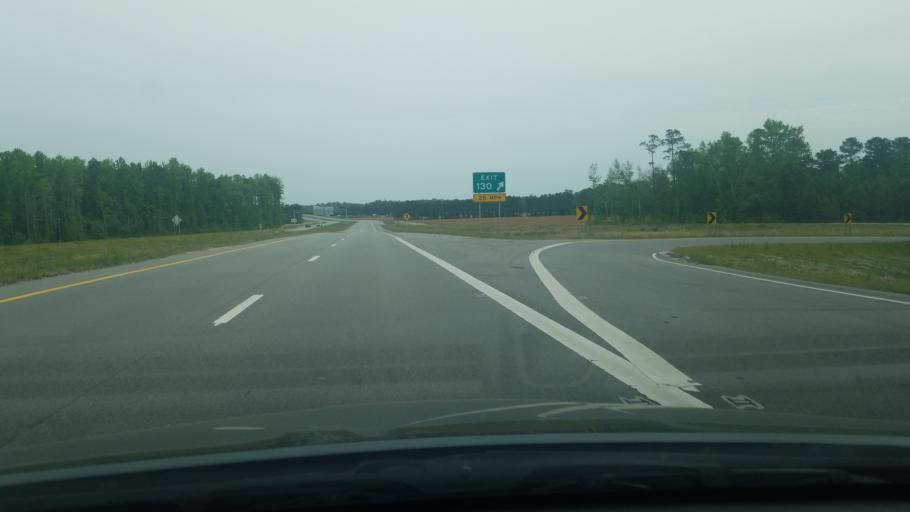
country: US
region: North Carolina
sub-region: Jones County
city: Maysville
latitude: 35.0002
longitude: -77.2323
